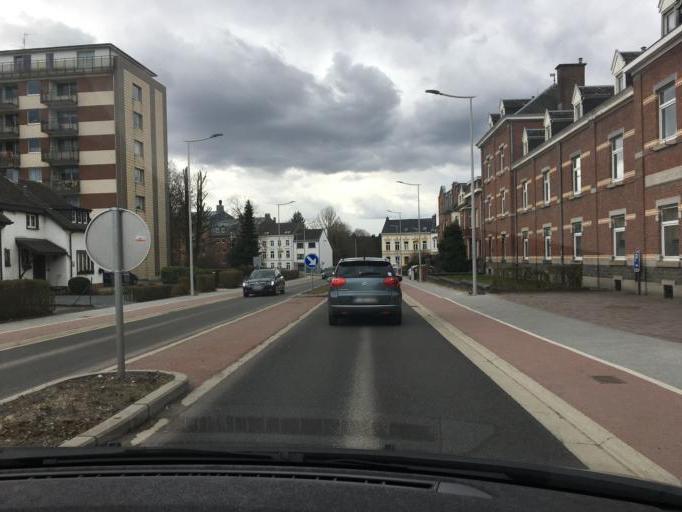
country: BE
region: Wallonia
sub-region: Province de Liege
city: Eupen
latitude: 50.6329
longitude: 6.0259
